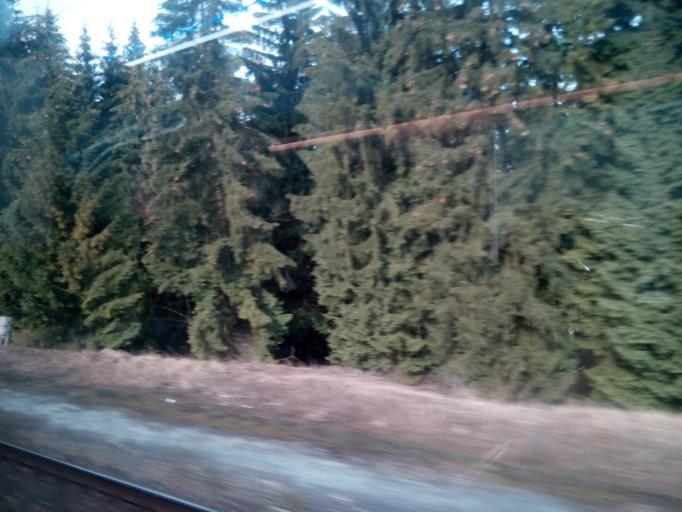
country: SK
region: Zilinsky
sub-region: Okres Liptovsky Mikulas
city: Hybe
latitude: 49.0499
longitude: 19.9153
